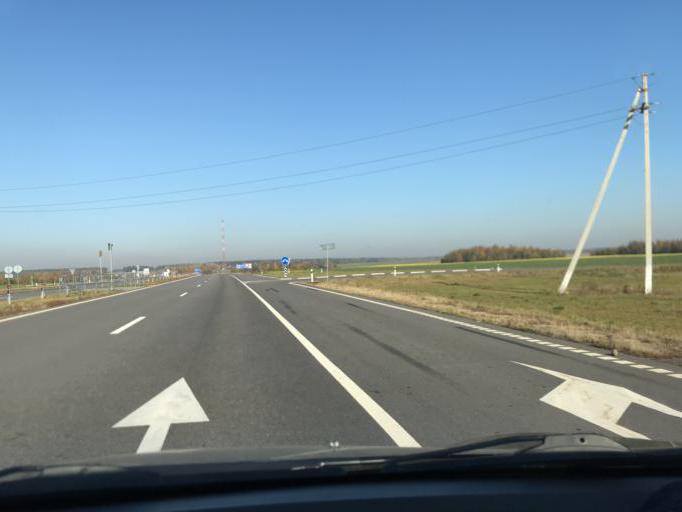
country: BY
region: Mogilev
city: Babruysk
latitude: 53.1715
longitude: 29.3602
